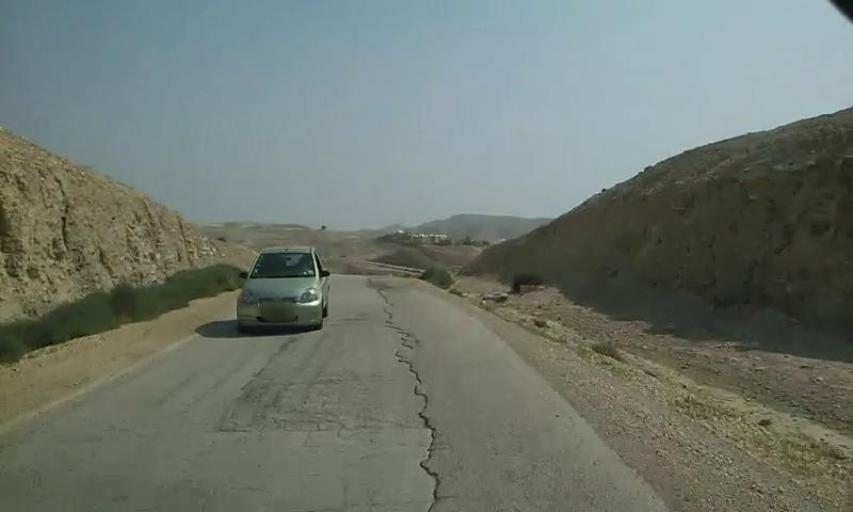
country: PS
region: West Bank
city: Jericho
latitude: 31.7917
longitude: 35.4277
